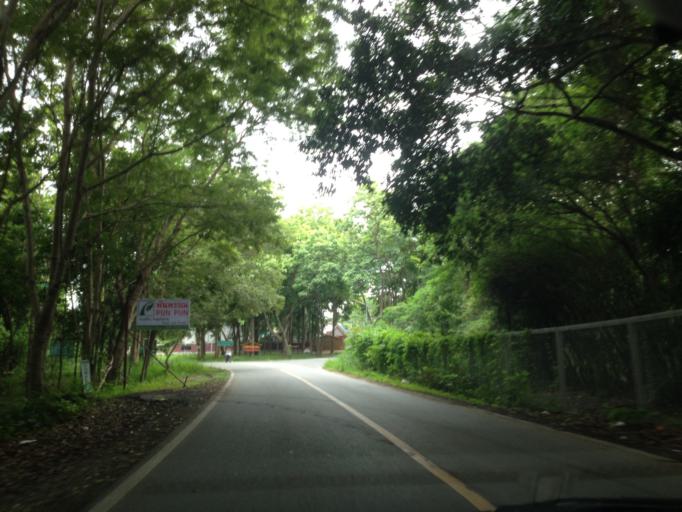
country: TH
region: Chiang Mai
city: Hang Dong
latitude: 18.7432
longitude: 98.9244
